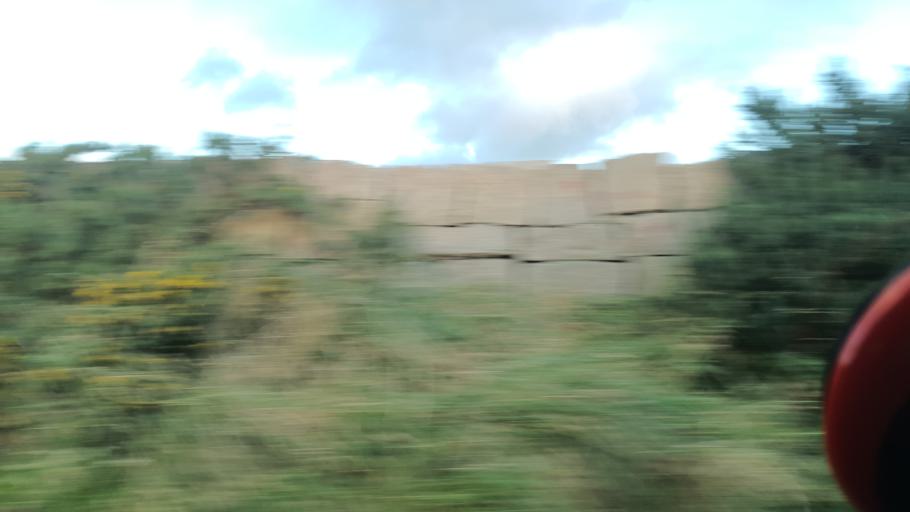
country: GB
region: Northern Ireland
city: Kilkeel
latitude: 54.0551
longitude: -6.0820
